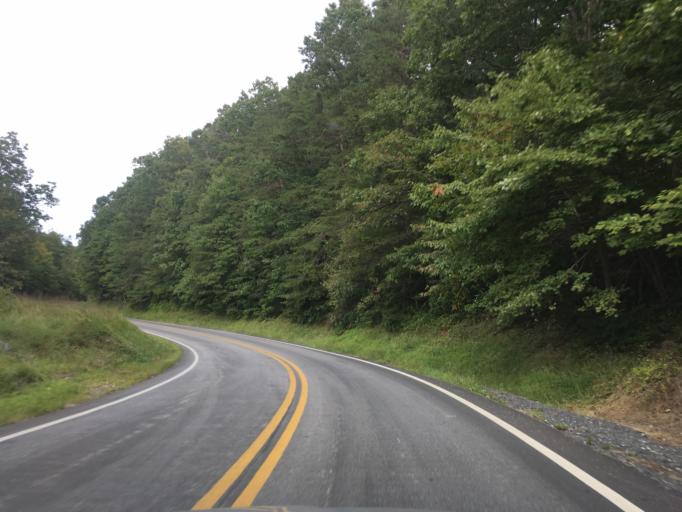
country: US
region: Pennsylvania
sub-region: York County
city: New Freedom
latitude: 39.6481
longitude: -76.7546
